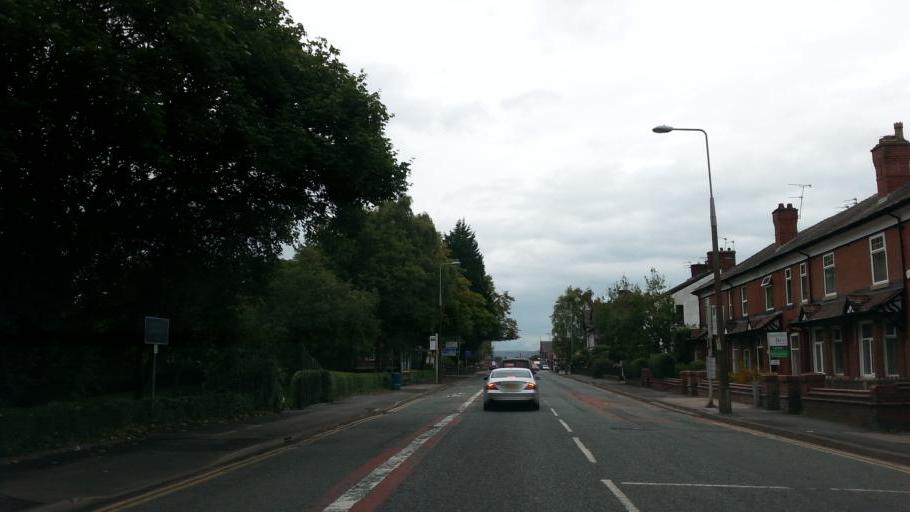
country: GB
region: England
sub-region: Borough of Bury
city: Whitefield
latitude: 53.5495
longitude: -2.2949
